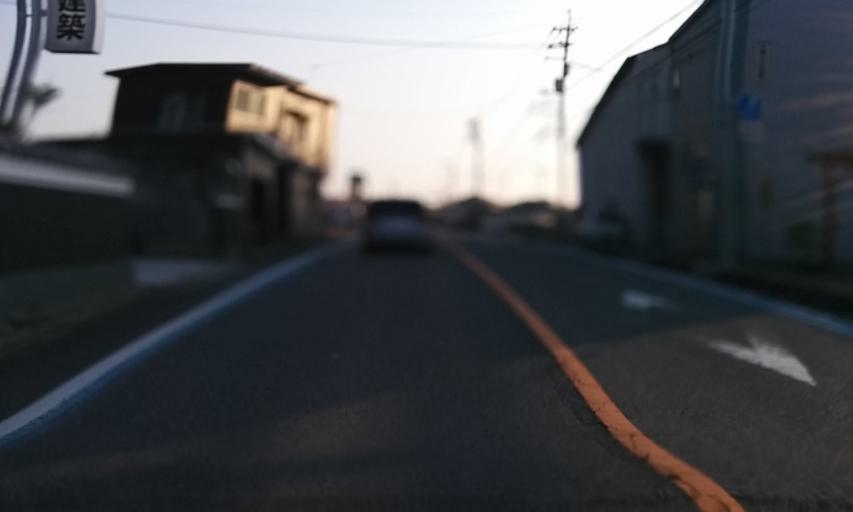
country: JP
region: Ehime
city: Masaki-cho
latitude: 33.7816
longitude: 132.7600
